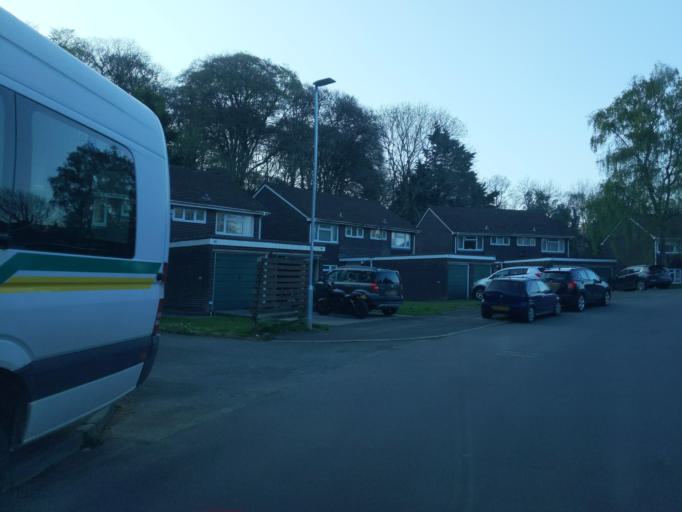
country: GB
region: England
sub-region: Plymouth
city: Plymstock
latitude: 50.3505
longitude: -4.0901
